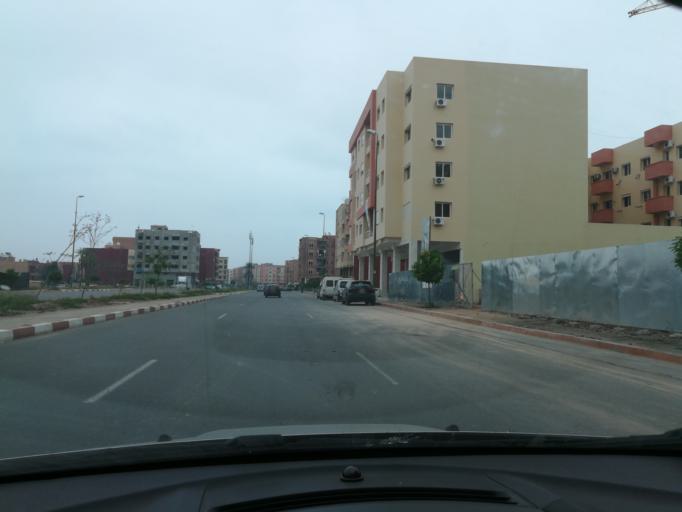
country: MA
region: Marrakech-Tensift-Al Haouz
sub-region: Marrakech
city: Marrakesh
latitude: 31.6672
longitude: -8.0301
